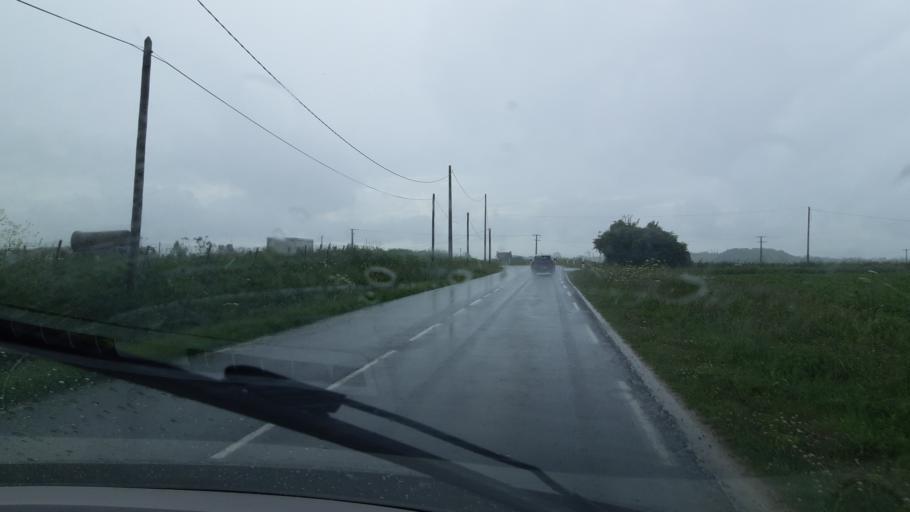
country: FR
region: Brittany
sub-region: Departement du Finistere
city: Saint-Pol-de-Leon
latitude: 48.6660
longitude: -4.0142
